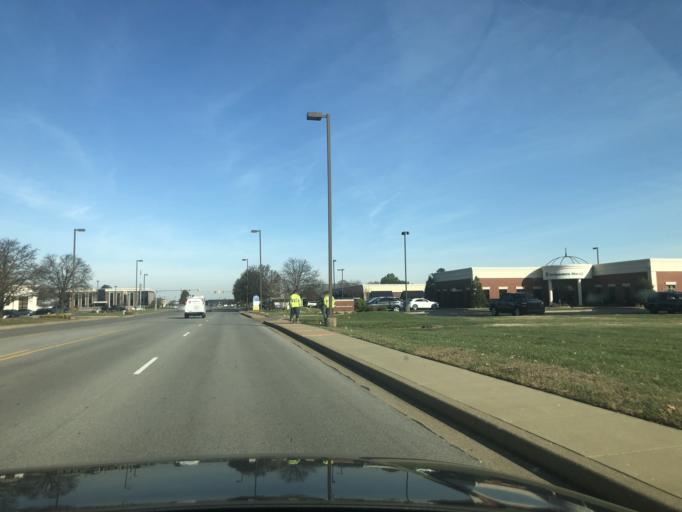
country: US
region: Indiana
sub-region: Warrick County
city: Newburgh
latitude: 37.9794
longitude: -87.4626
